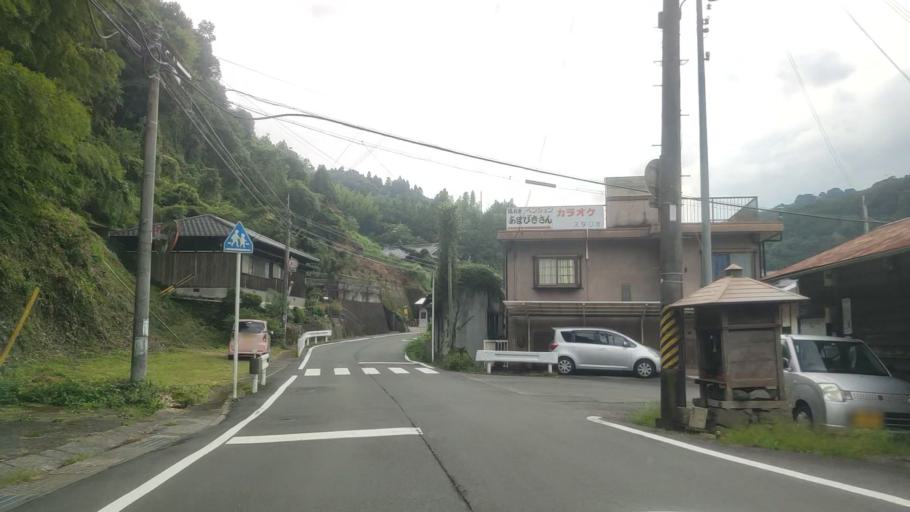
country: JP
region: Wakayama
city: Hashimoto
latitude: 34.2695
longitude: 135.5551
